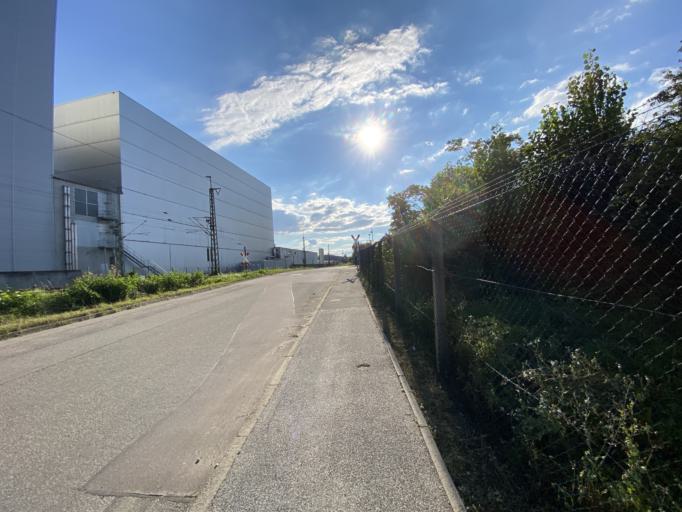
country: DE
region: Bavaria
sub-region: Lower Bavaria
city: Dingolfing
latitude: 48.6414
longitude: 12.4795
